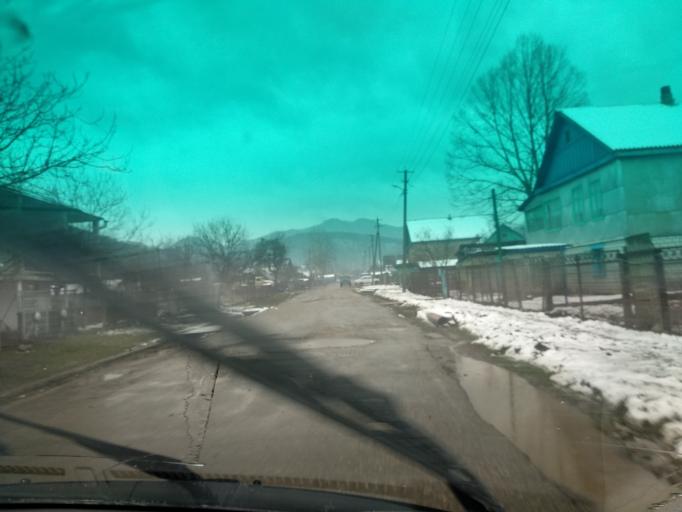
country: RU
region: Krasnodarskiy
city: Khadyzhensk
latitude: 44.2107
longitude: 39.4269
